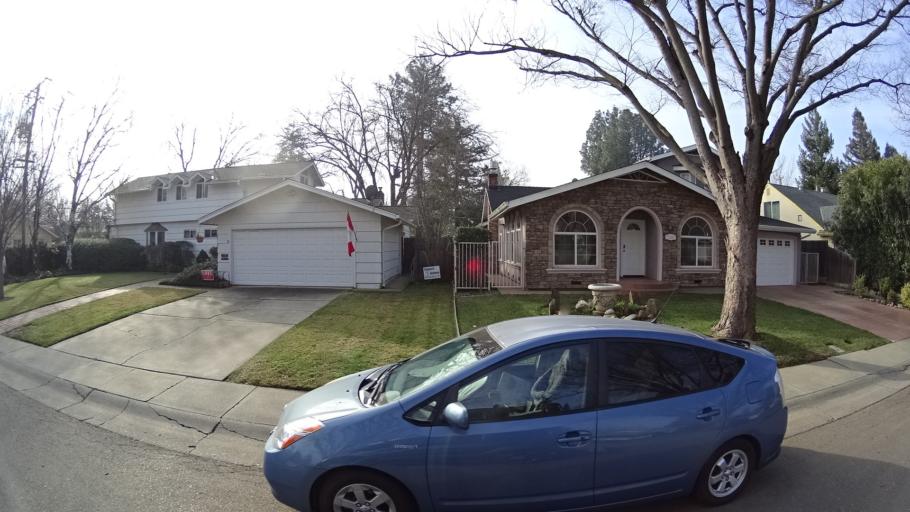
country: US
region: California
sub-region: Yolo County
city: Davis
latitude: 38.5526
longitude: -121.7633
